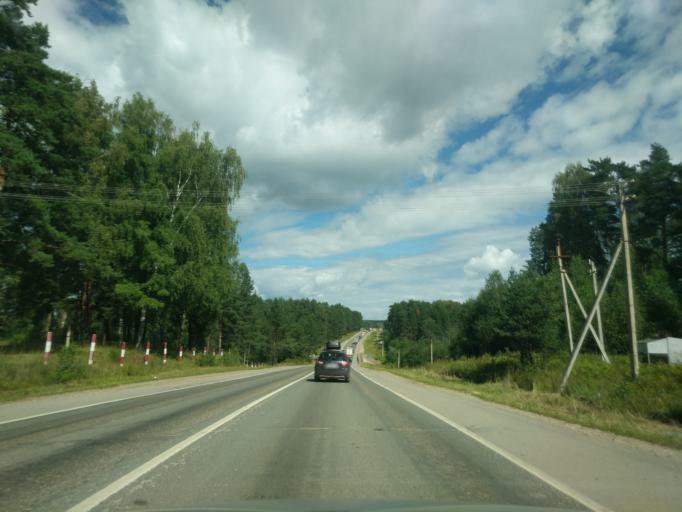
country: RU
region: Jaroslavl
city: Levashevo
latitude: 57.6704
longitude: 40.5801
